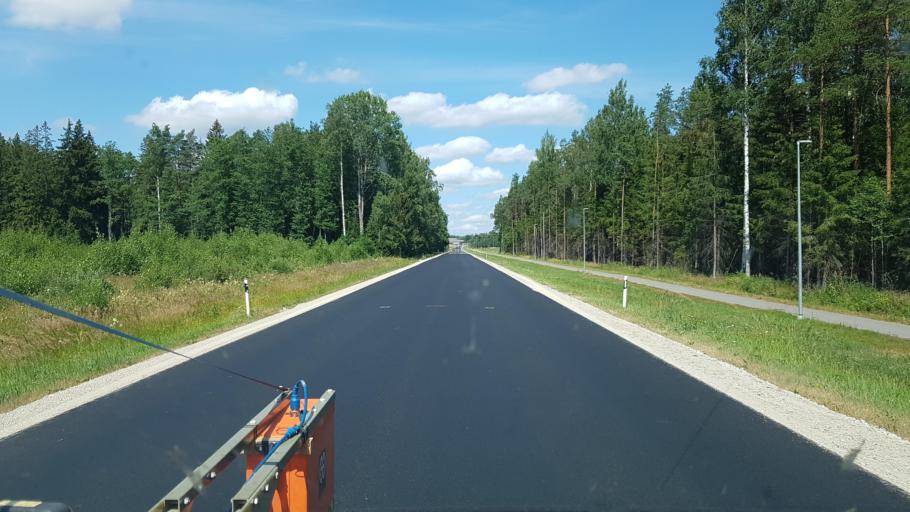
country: EE
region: Paernumaa
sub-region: Tootsi vald
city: Tootsi
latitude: 58.4956
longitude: 24.8046
